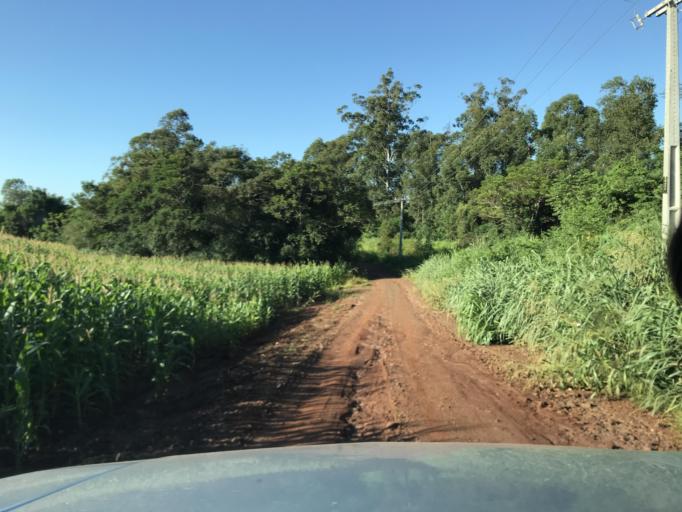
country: BR
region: Parana
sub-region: Palotina
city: Palotina
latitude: -24.2198
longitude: -53.7485
